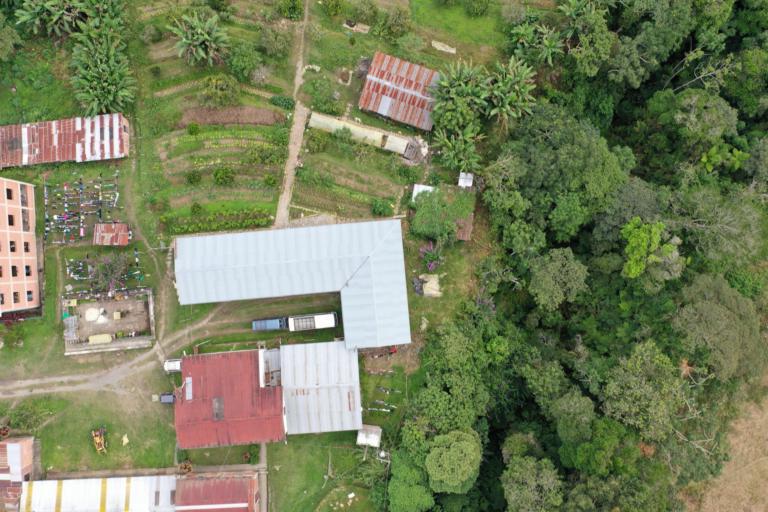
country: BO
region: La Paz
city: Coroico
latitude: -16.2583
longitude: -67.6925
